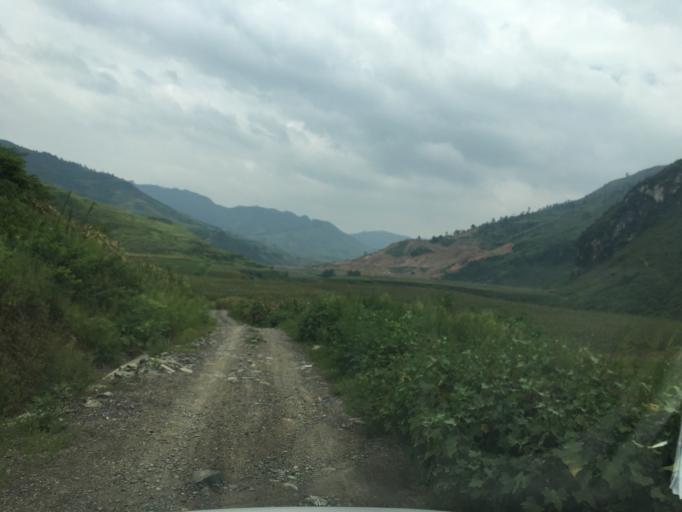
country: CN
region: Guangxi Zhuangzu Zizhiqu
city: Xinzhou
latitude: 25.1787
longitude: 105.7322
